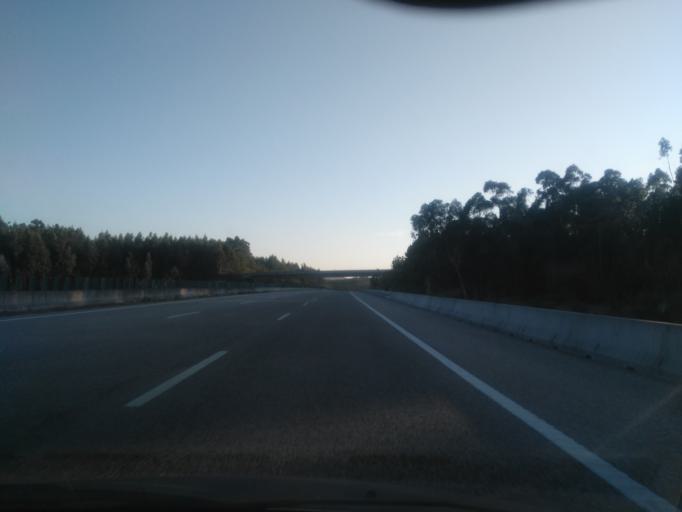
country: PT
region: Coimbra
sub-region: Figueira da Foz
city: Lavos
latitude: 40.0775
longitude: -8.7744
